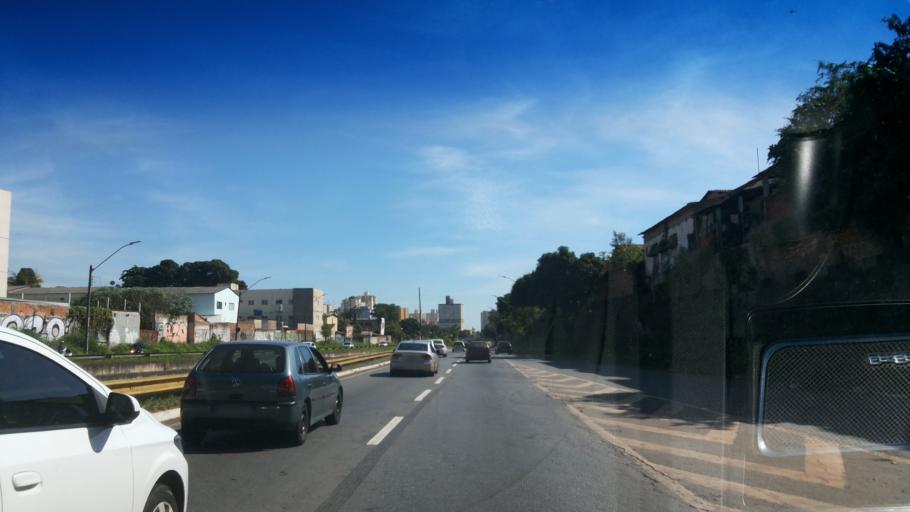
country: BR
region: Goias
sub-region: Goiania
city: Goiania
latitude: -16.6850
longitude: -49.2461
